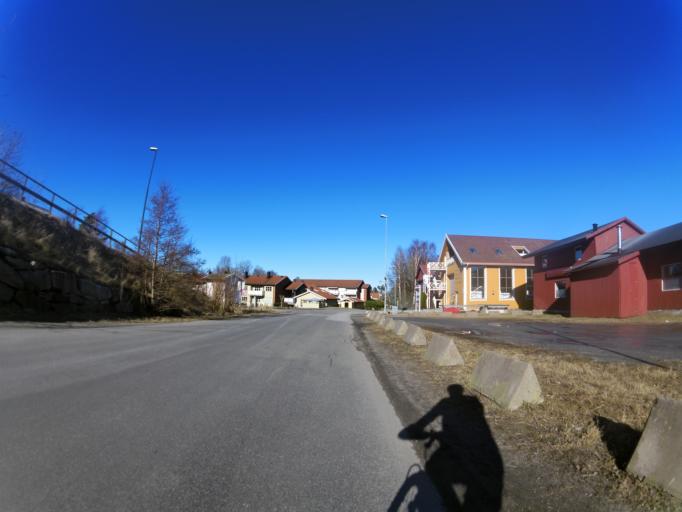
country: NO
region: Ostfold
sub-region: Fredrikstad
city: Fredrikstad
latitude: 59.2128
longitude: 10.9072
